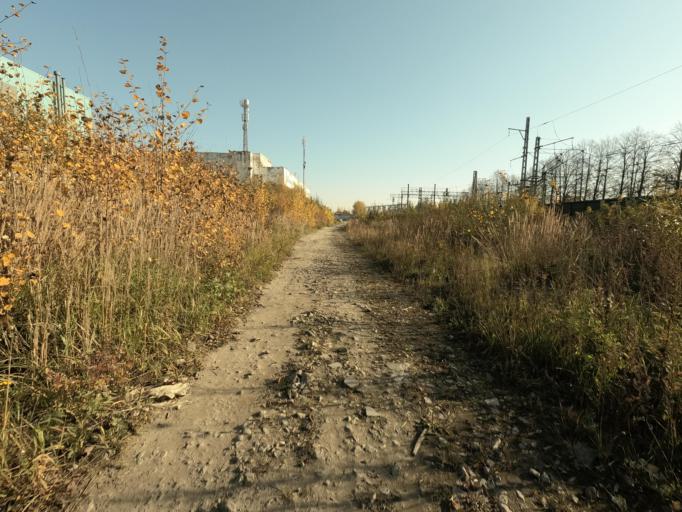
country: RU
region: St.-Petersburg
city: Obukhovo
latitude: 59.8429
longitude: 30.4710
